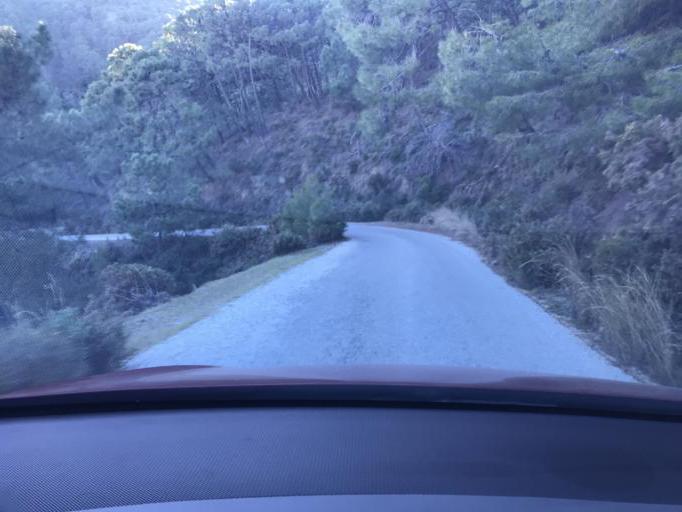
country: ES
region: Andalusia
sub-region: Provincia de Malaga
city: Tolox
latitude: 36.6835
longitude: -4.9182
